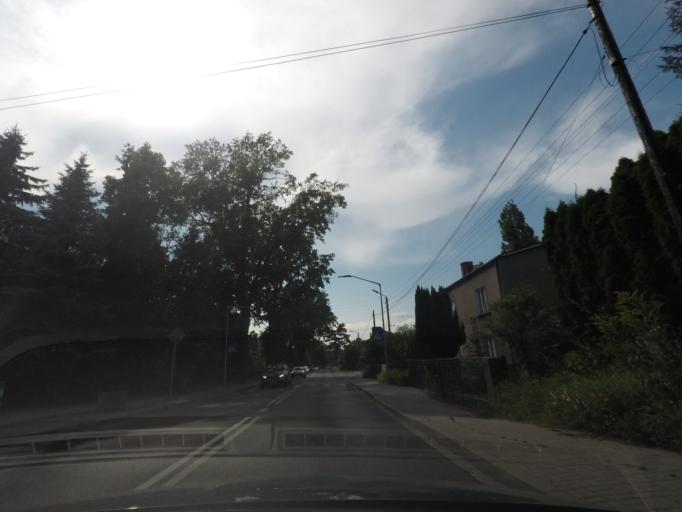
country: PL
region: Lesser Poland Voivodeship
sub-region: Powiat oswiecimski
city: Brzeszcze
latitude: 49.9723
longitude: 19.1318
